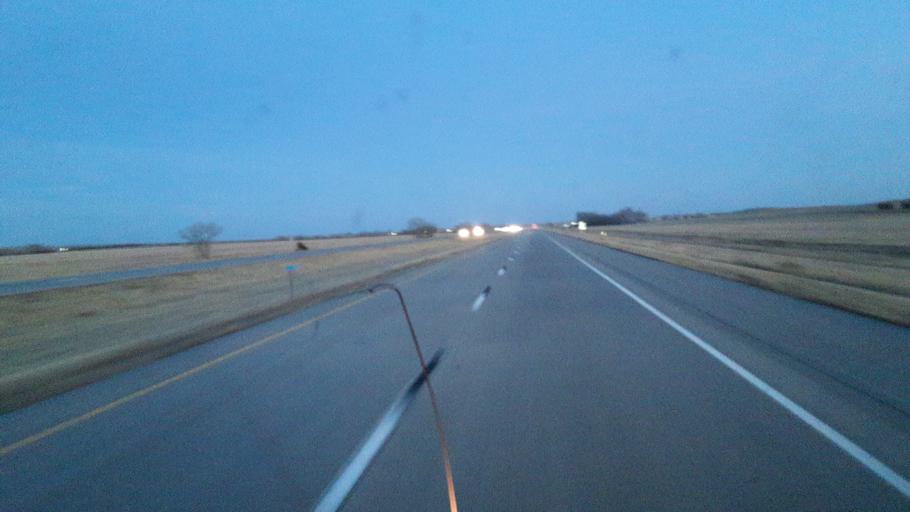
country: US
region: Nebraska
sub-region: Keith County
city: Ogallala
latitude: 41.1087
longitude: -101.5026
